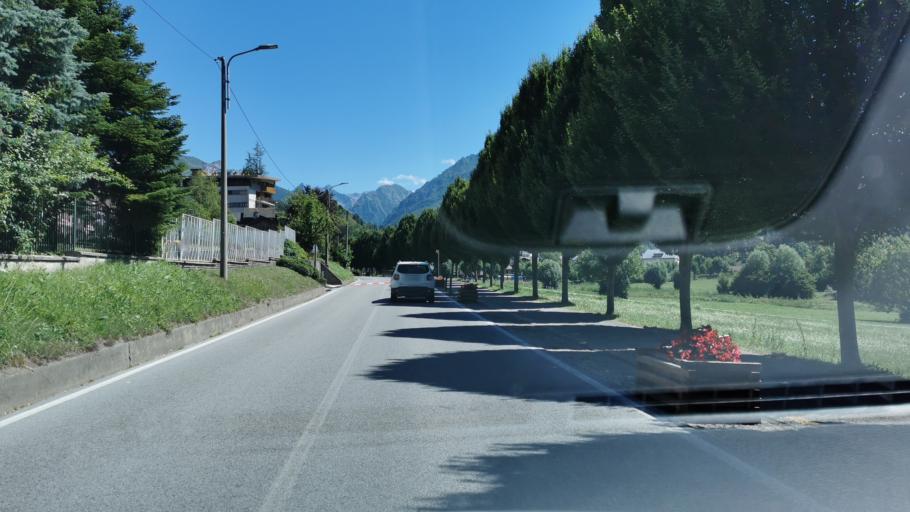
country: IT
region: Piedmont
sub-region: Provincia di Cuneo
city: Entracque
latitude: 44.2457
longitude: 7.3948
